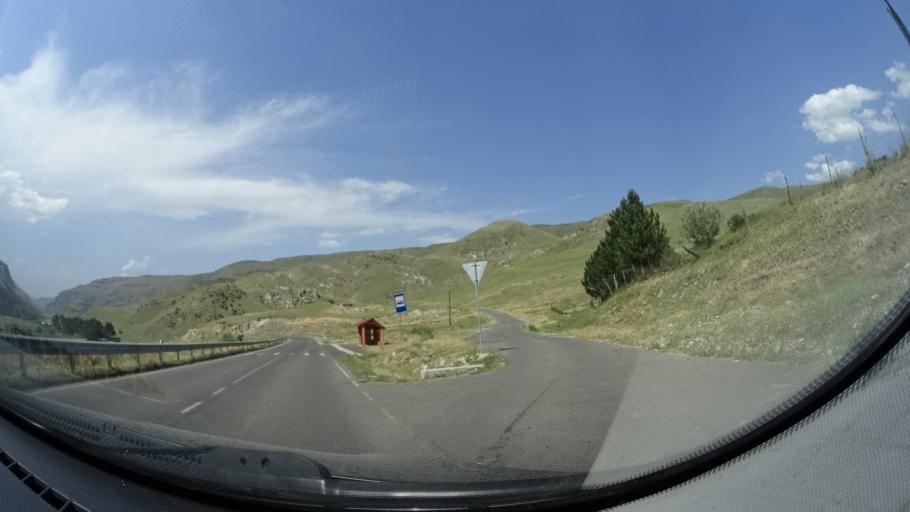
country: GE
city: Akhalk'alak'i
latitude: 41.4184
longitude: 43.3246
